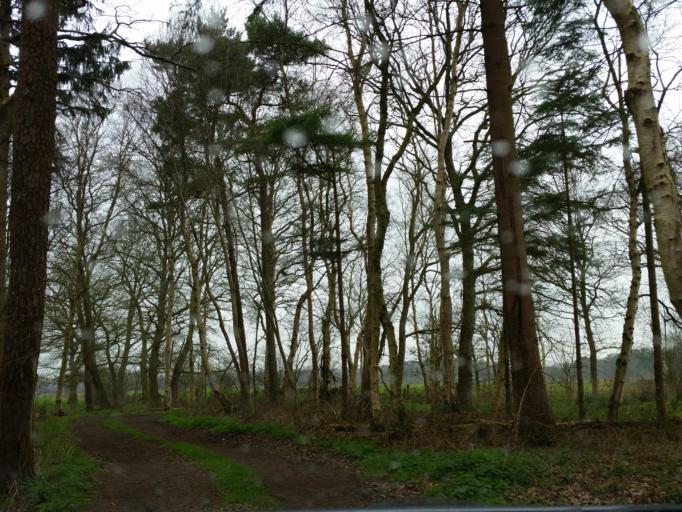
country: DE
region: Lower Saxony
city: Mittelstenahe
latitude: 53.6009
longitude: 8.9860
